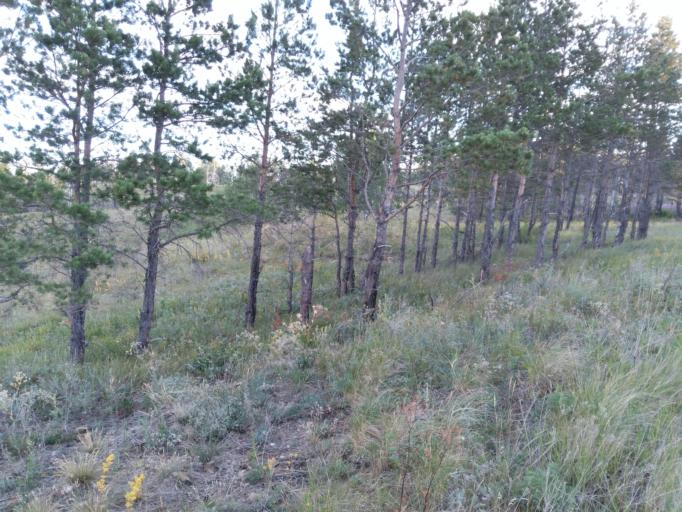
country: RU
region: Bashkortostan
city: Uchaly
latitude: 54.3226
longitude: 59.3916
